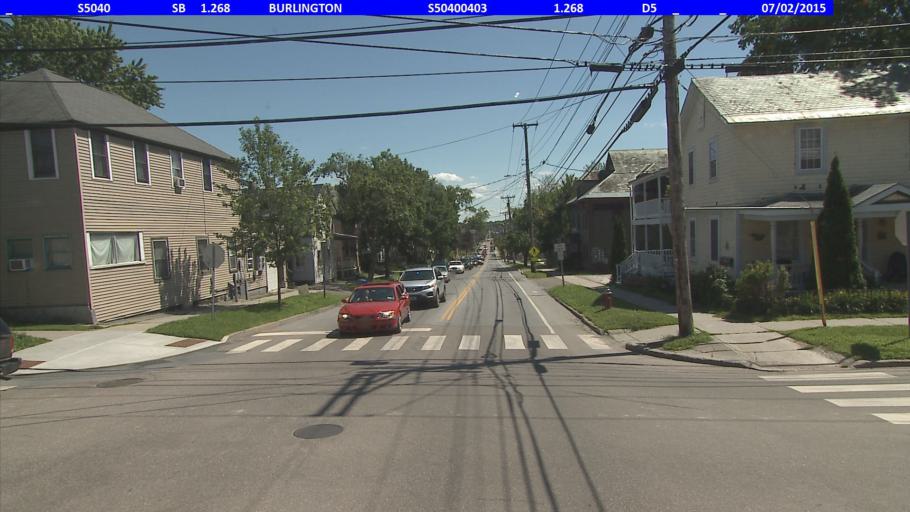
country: US
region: Vermont
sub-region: Chittenden County
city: Burlington
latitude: 44.4736
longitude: -73.2154
